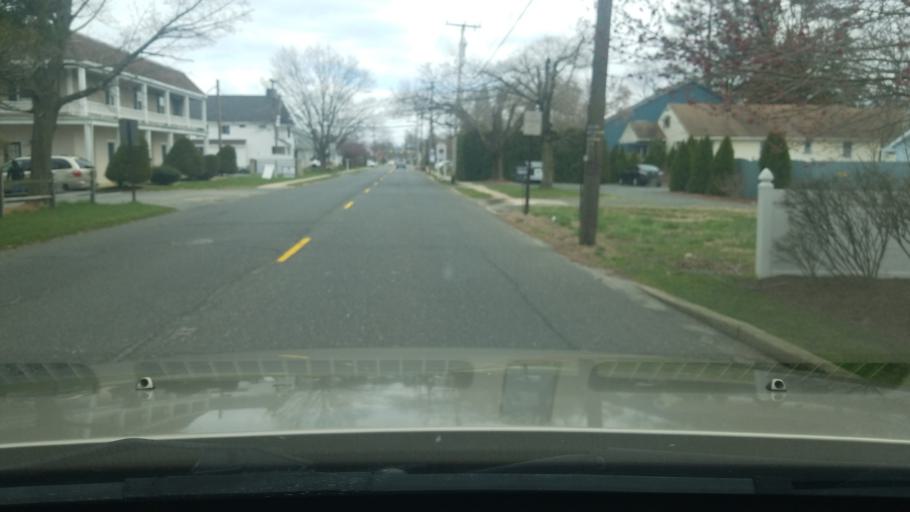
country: US
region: New Jersey
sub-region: Monmouth County
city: Manasquan
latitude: 40.1290
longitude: -74.0562
